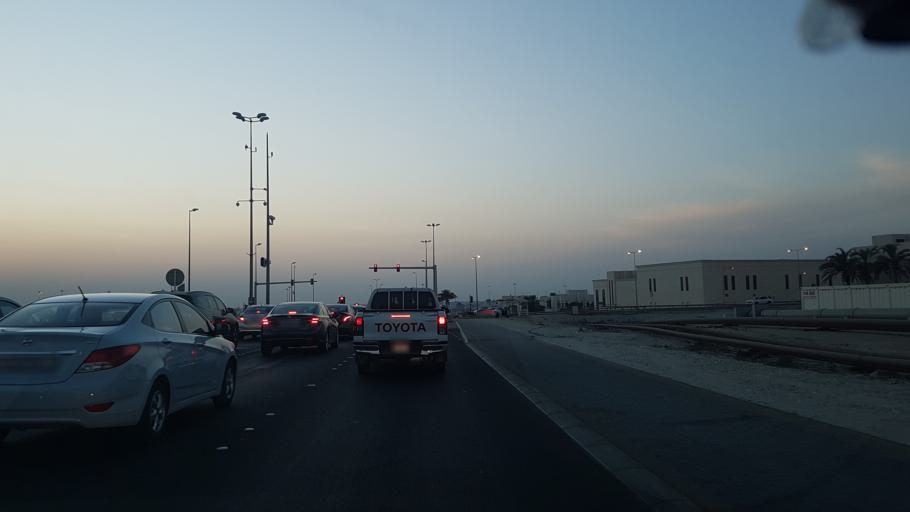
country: BH
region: Central Governorate
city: Madinat Hamad
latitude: 26.1387
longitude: 50.5183
